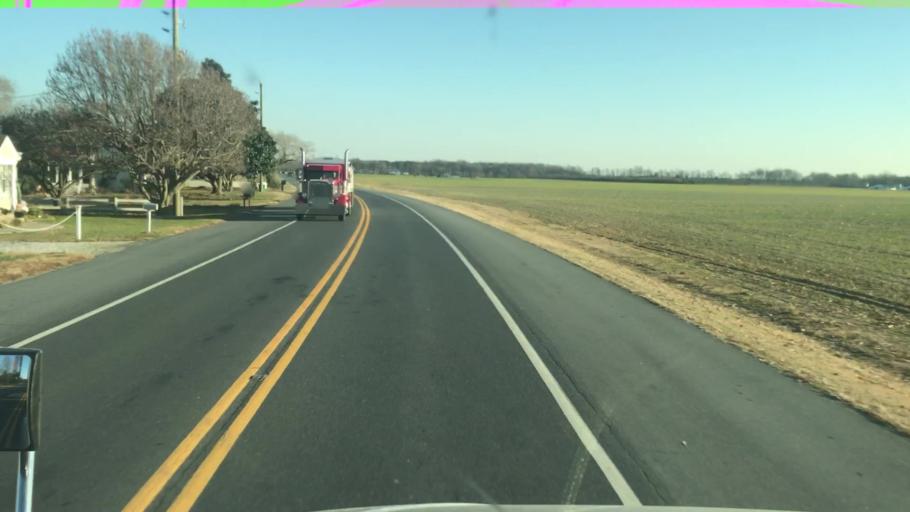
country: US
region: Delaware
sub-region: Sussex County
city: Bridgeville
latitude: 38.7903
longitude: -75.6884
